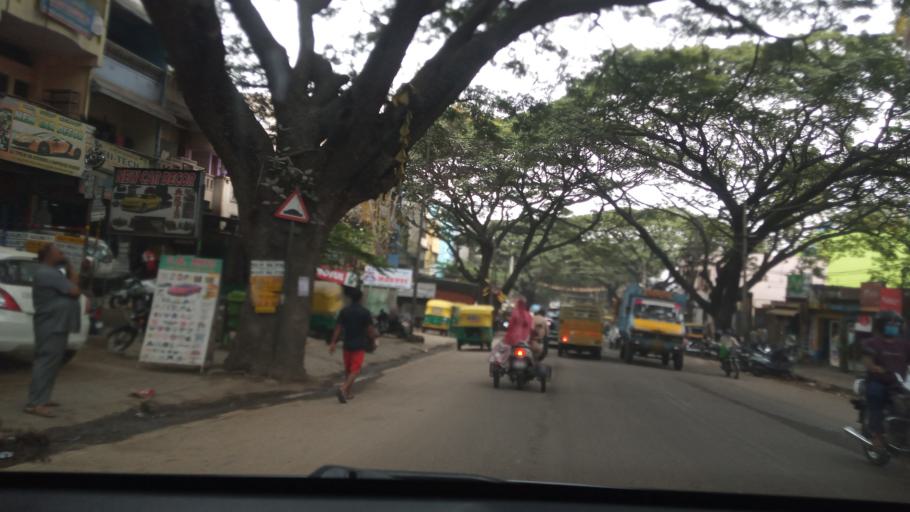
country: IN
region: Karnataka
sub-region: Bangalore Urban
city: Bangalore
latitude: 13.0212
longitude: 77.5360
